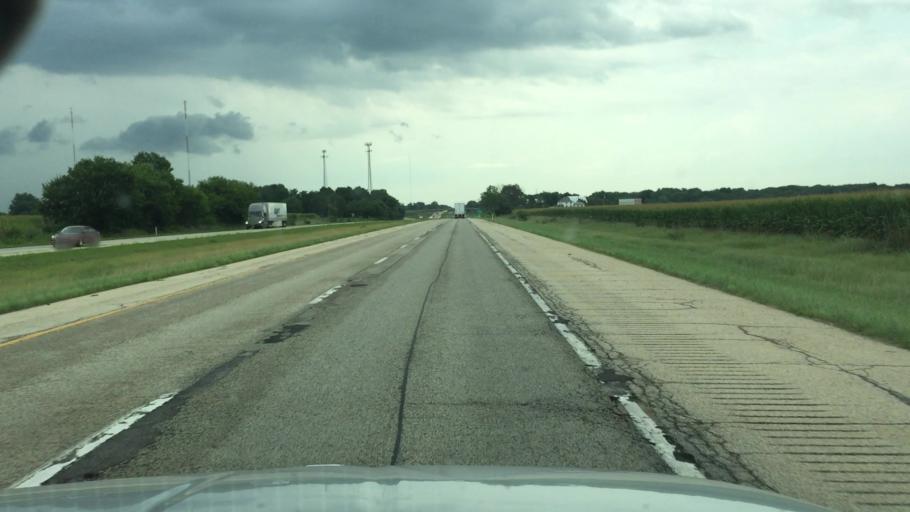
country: US
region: Illinois
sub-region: Peoria County
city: Hanna City
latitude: 40.7789
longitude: -89.7653
